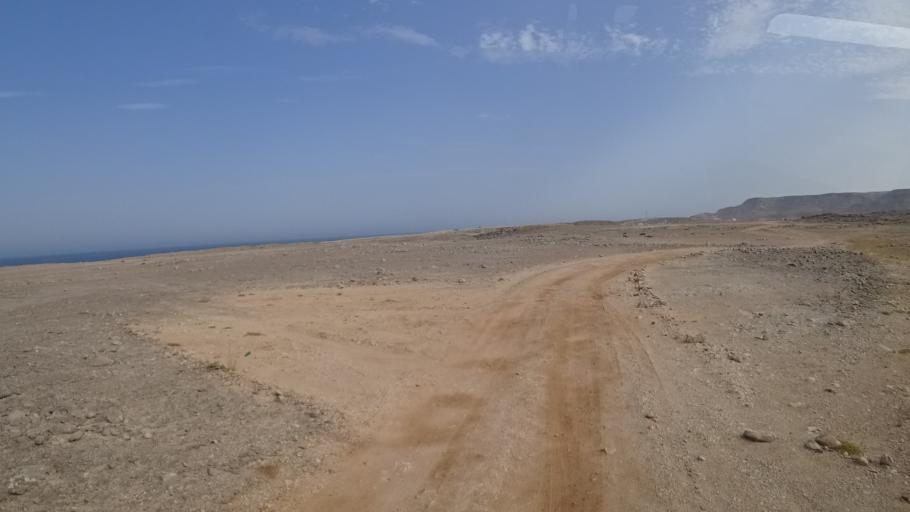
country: OM
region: Ash Sharqiyah
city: Sur
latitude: 22.4548
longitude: 59.8253
